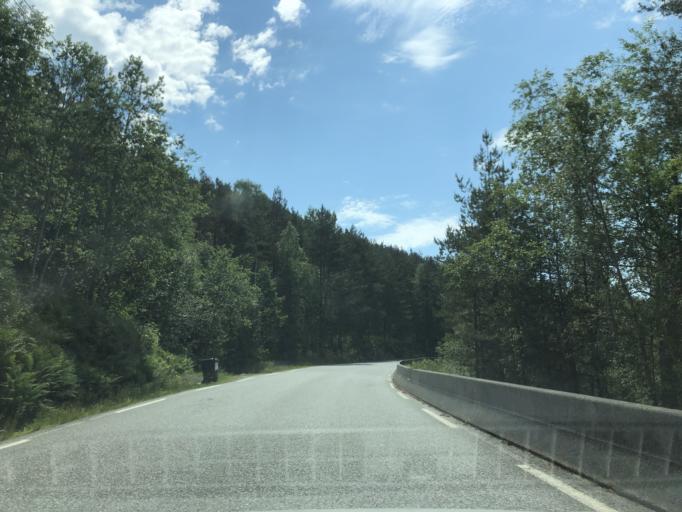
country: NO
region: Hordaland
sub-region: Jondal
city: Jondal
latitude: 60.2977
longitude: 6.2432
